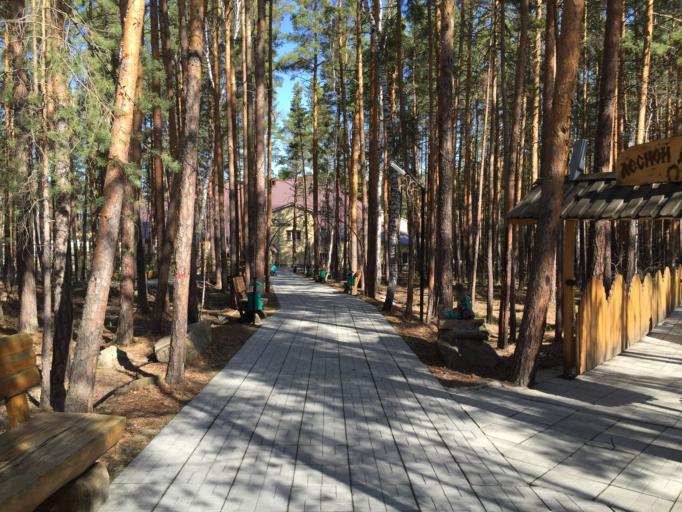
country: RU
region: Chelyabinsk
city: Kyshtym
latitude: 55.6159
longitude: 60.6371
